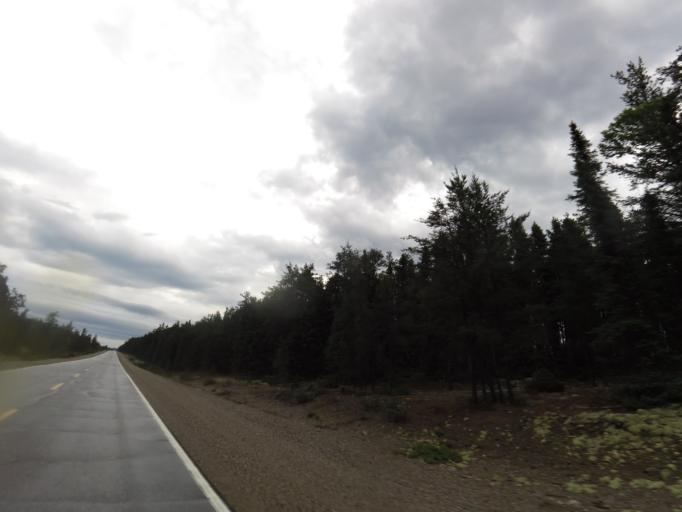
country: CA
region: Quebec
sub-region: Abitibi-Temiscamingue
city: Amos
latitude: 48.9229
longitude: -77.9443
